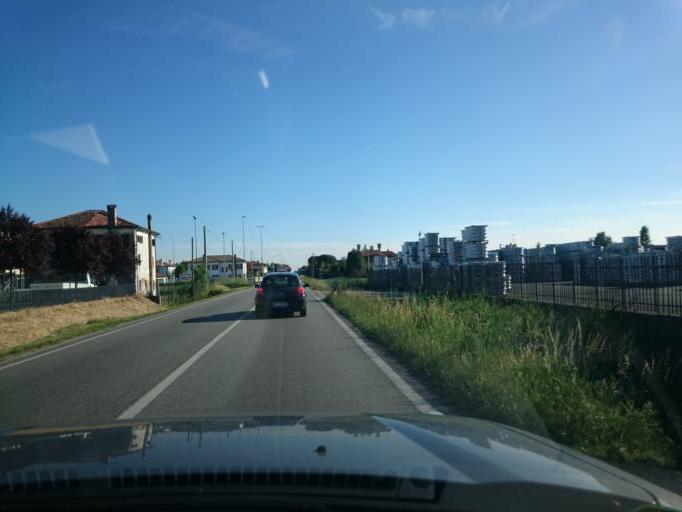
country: IT
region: Veneto
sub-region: Provincia di Venezia
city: Caselle
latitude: 45.5037
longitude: 12.0108
